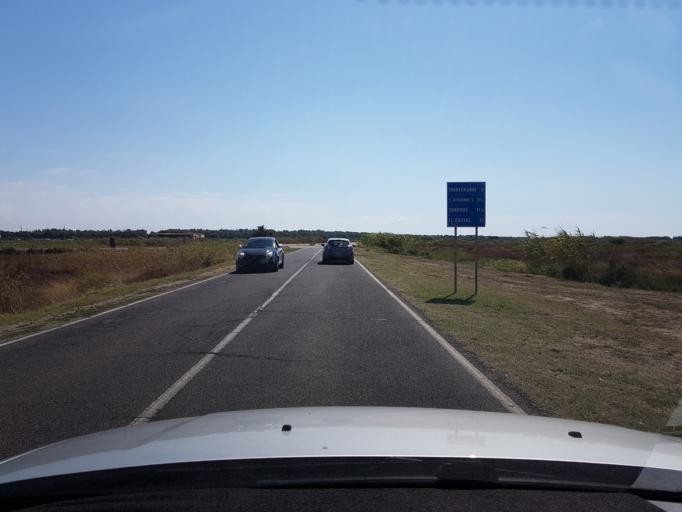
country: IT
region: Sardinia
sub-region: Provincia di Oristano
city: Cabras
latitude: 39.9201
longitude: 8.5217
